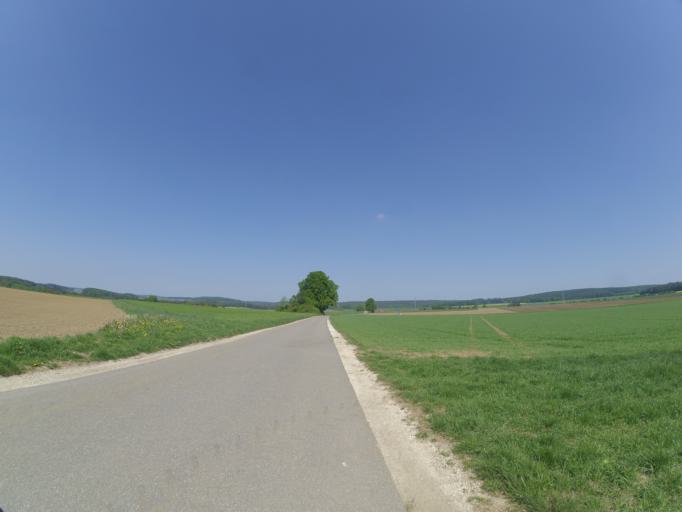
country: DE
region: Baden-Wuerttemberg
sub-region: Tuebingen Region
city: Berghulen
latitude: 48.4696
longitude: 9.8340
